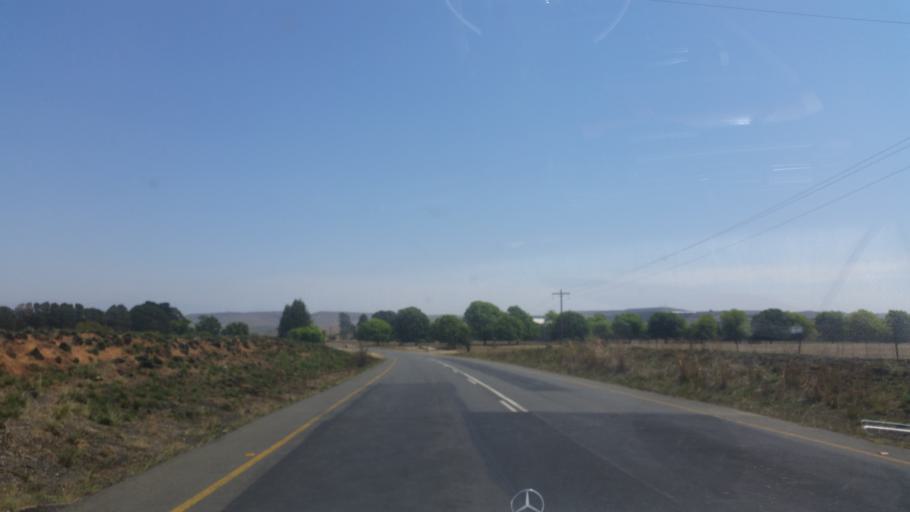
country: ZA
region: KwaZulu-Natal
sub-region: uMgungundlovu District Municipality
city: Mooirivier
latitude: -29.1486
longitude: 29.9781
